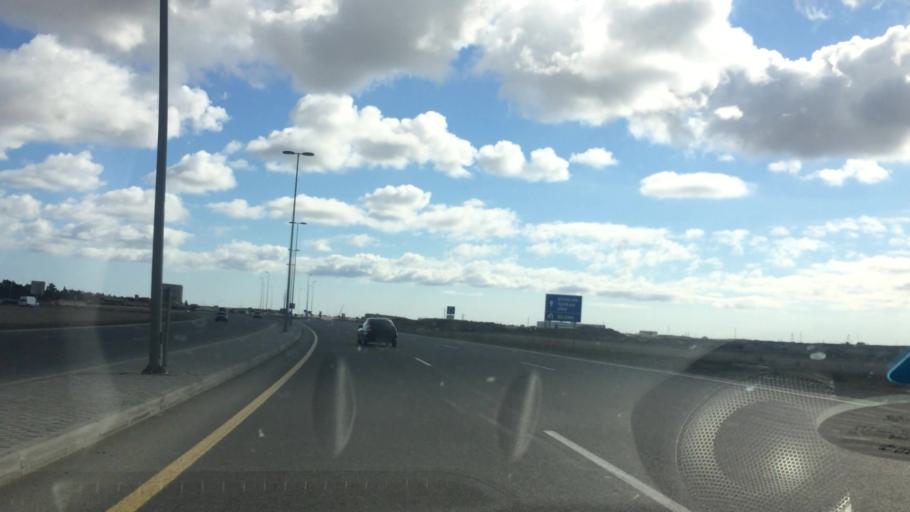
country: AZ
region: Baki
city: Mardakyany
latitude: 40.4587
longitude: 50.1296
